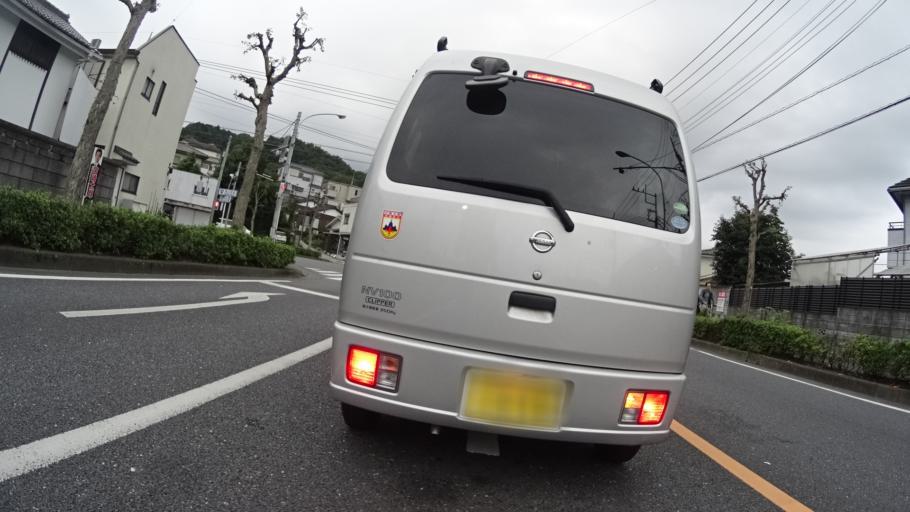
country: JP
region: Tokyo
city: Fussa
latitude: 35.7714
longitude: 139.2925
